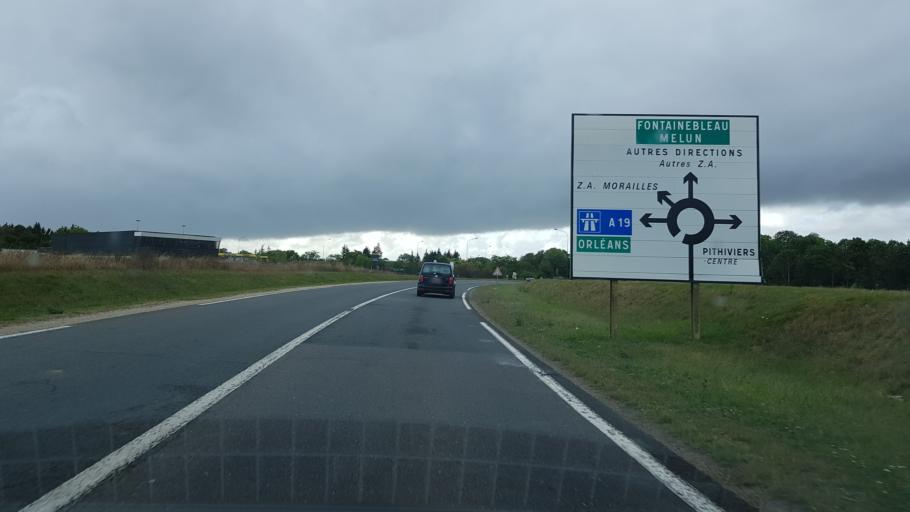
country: FR
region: Centre
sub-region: Departement du Loiret
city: Pithiviers
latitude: 48.1593
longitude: 2.2372
